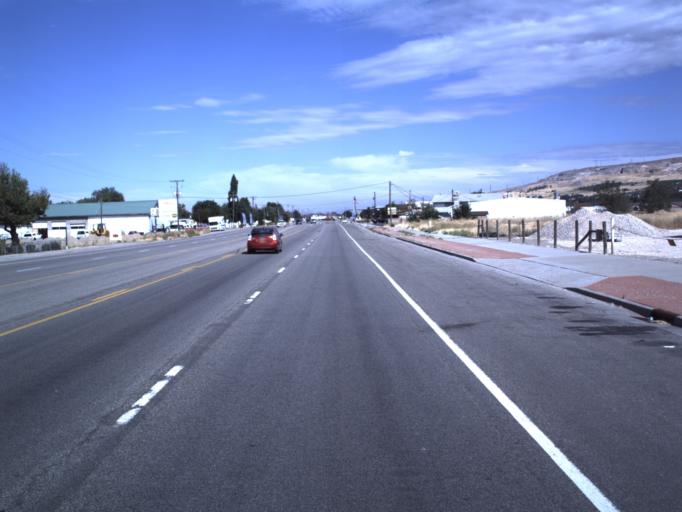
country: US
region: Utah
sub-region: Weber County
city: Pleasant View
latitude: 41.2997
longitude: -111.9991
